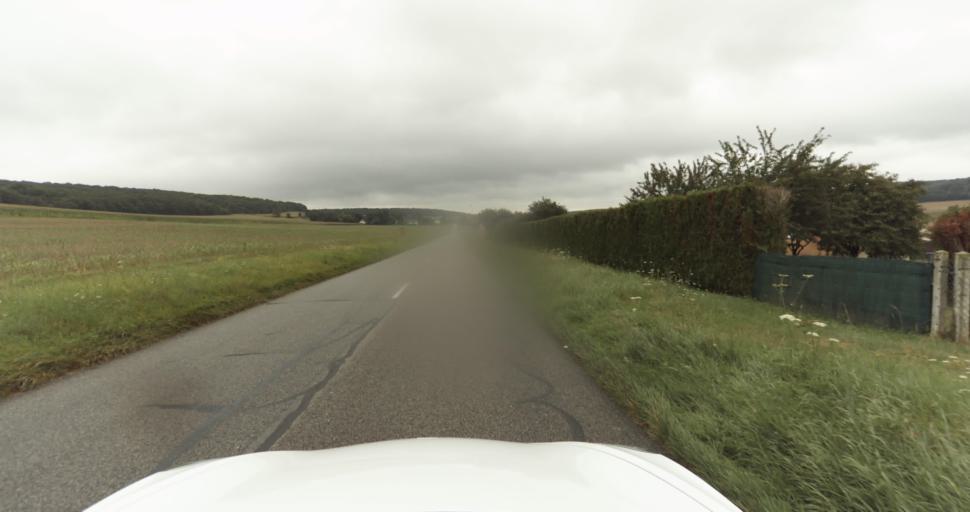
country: FR
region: Haute-Normandie
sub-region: Departement de l'Eure
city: Normanville
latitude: 49.0760
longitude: 1.1659
